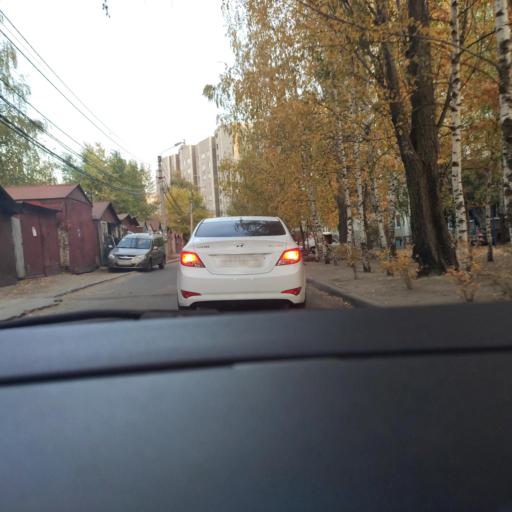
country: RU
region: Voronezj
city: Podgornoye
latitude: 51.7000
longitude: 39.1369
